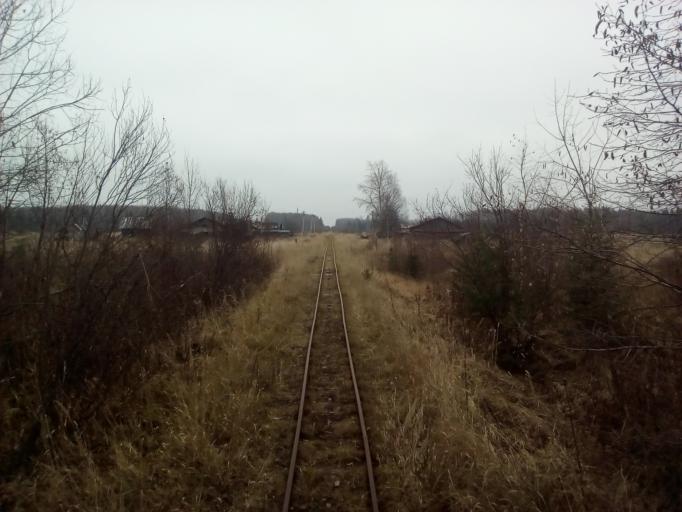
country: RU
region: Vologda
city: Kharovsk
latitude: 59.8028
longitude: 40.4564
